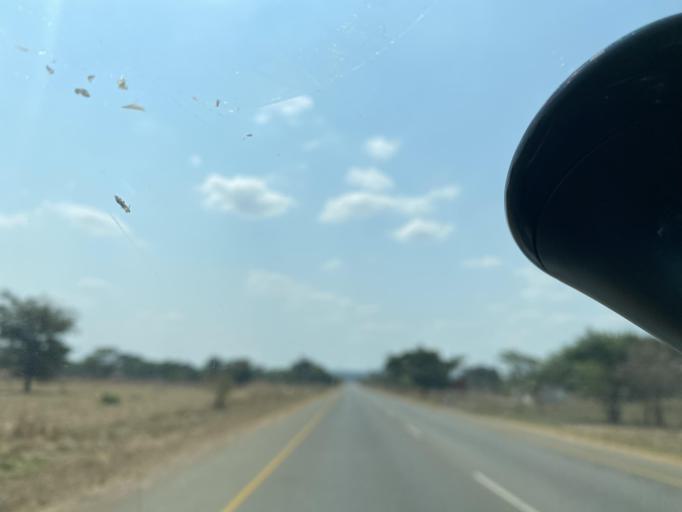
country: ZM
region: Lusaka
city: Chongwe
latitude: -15.5627
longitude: 28.6881
